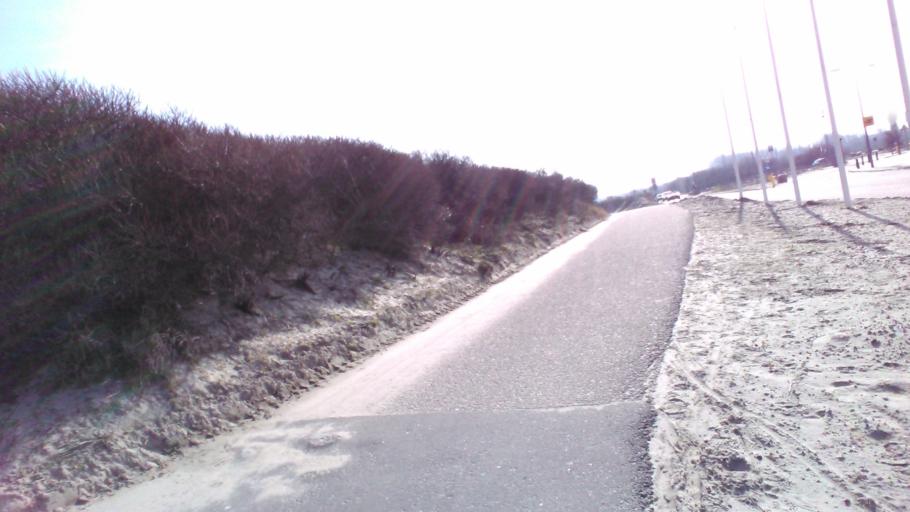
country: NL
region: South Holland
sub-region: Gemeente Rotterdam
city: Hoek van Holland
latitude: 51.9867
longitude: 4.1056
